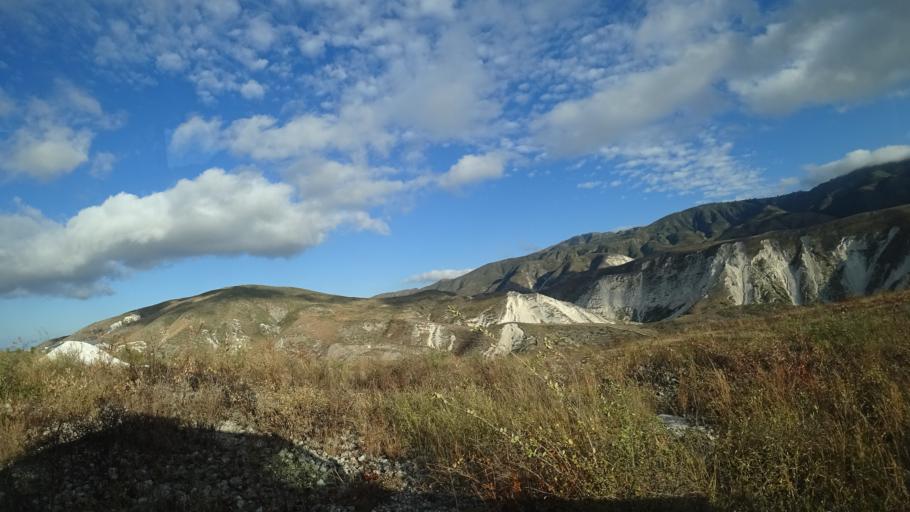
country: HT
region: Ouest
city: Croix des Bouquets
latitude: 18.6732
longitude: -72.2584
